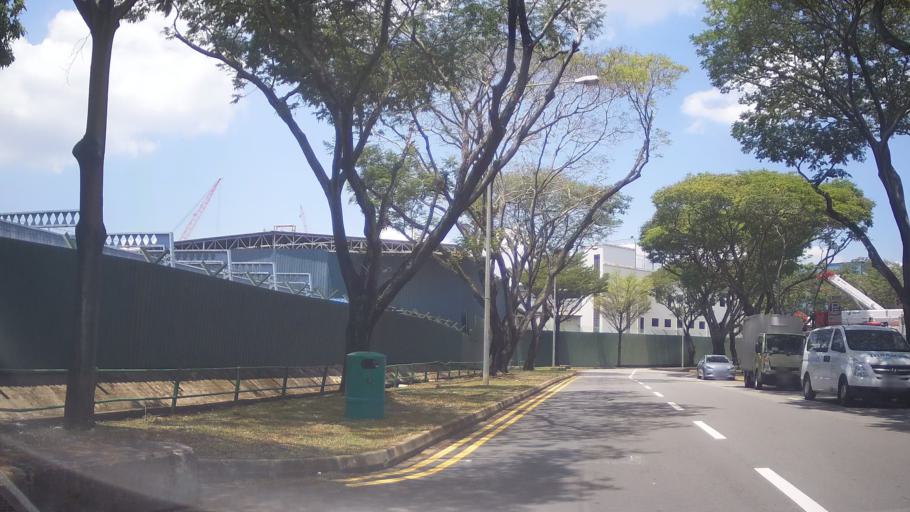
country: SG
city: Singapore
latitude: 1.3024
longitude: 103.6769
